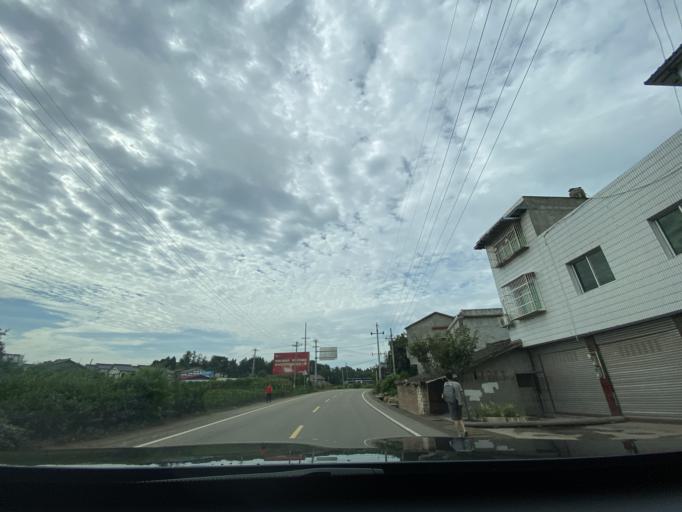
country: CN
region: Sichuan
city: Jiancheng
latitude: 30.4620
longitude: 104.6299
